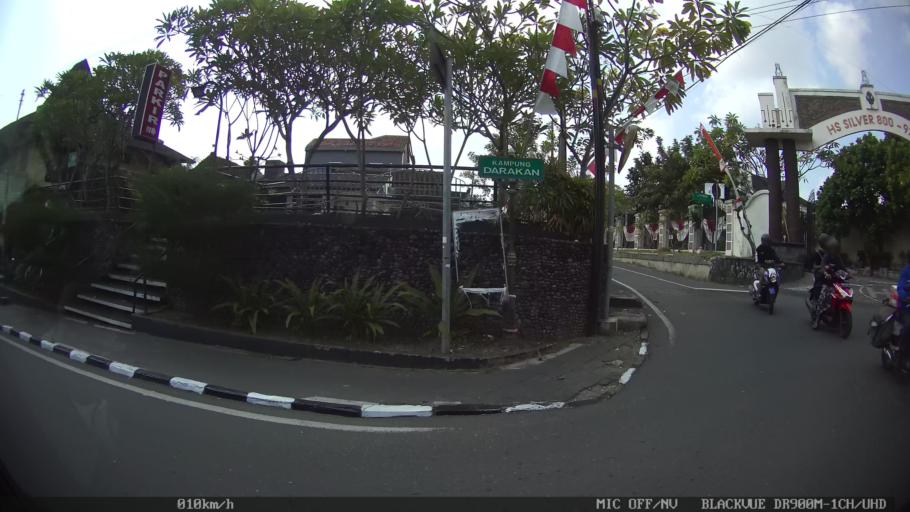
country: ID
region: Daerah Istimewa Yogyakarta
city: Yogyakarta
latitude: -7.8273
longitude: 110.3948
